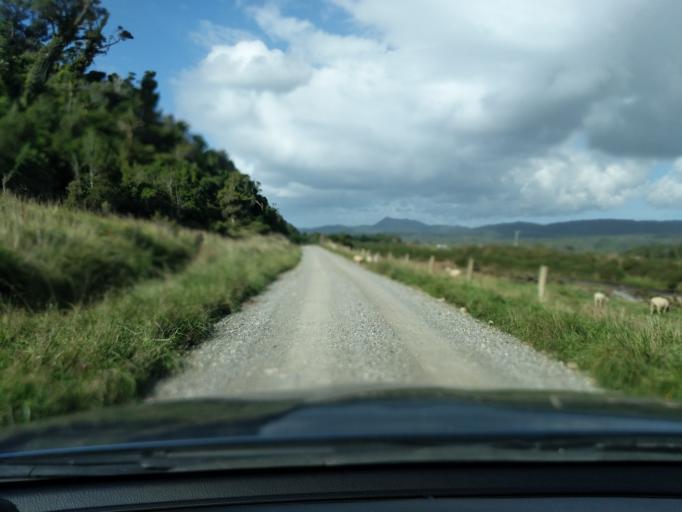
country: NZ
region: Tasman
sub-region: Tasman District
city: Takaka
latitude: -40.6540
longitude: 172.4564
